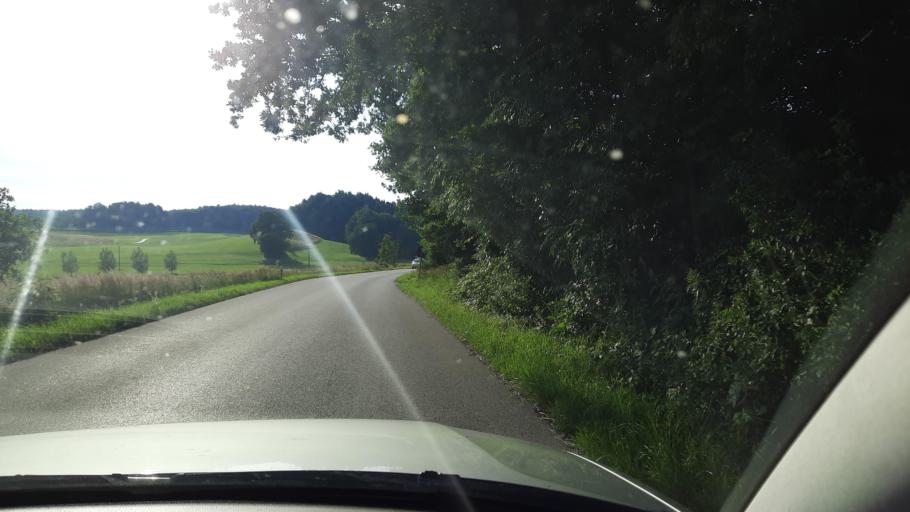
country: DE
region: Bavaria
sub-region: Upper Bavaria
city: Glonn
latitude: 47.9740
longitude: 11.8814
